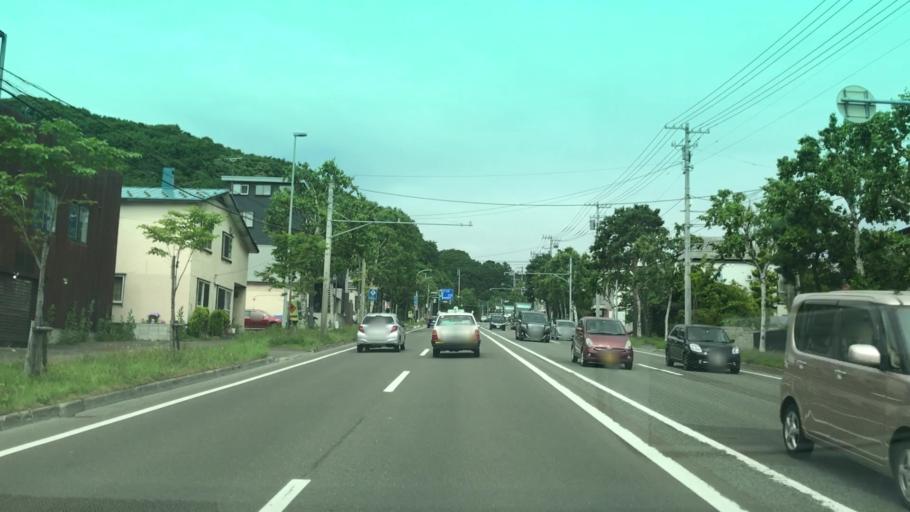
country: JP
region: Hokkaido
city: Sapporo
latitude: 43.0632
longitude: 141.2922
